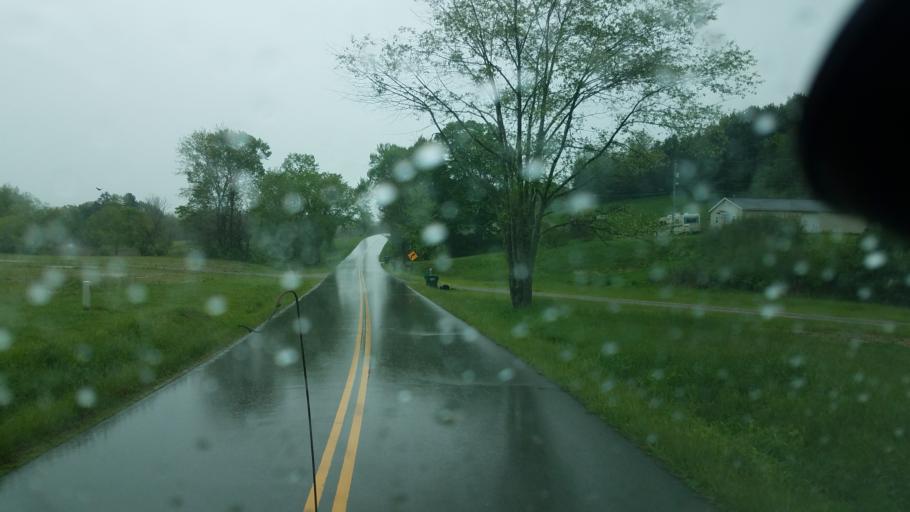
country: US
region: Ohio
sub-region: Muskingum County
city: Frazeysburg
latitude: 40.1366
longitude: -82.1127
